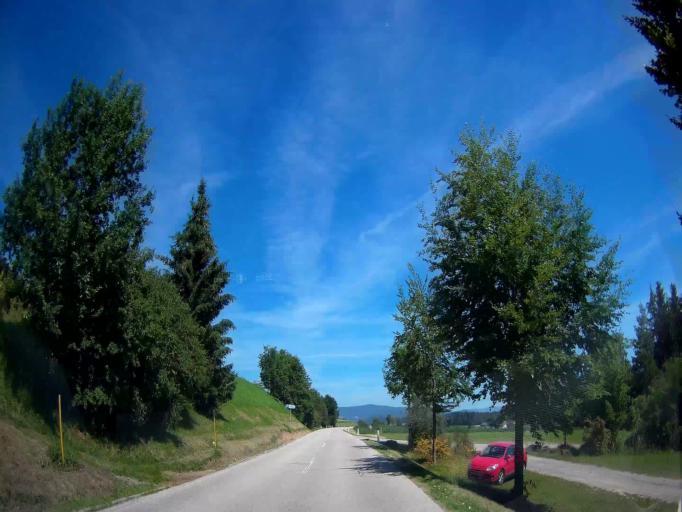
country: AT
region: Carinthia
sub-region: Politischer Bezirk Sankt Veit an der Glan
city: St. Georgen am Laengsee
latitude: 46.7905
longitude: 14.4188
